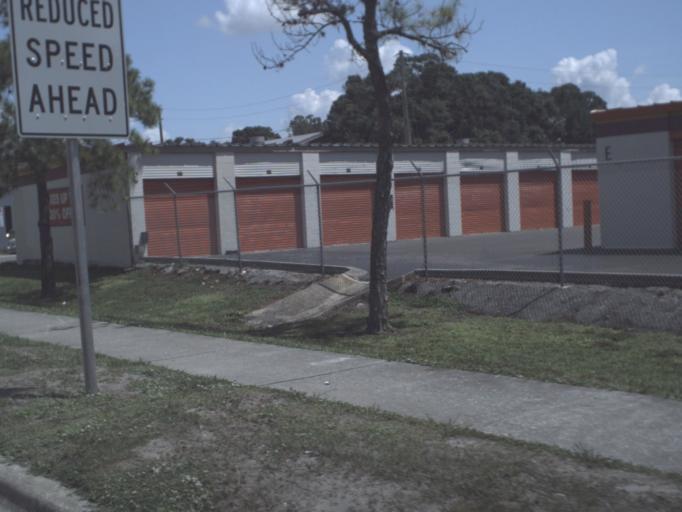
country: US
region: Florida
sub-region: Pinellas County
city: Saint Petersburg
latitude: 27.7570
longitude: -82.6793
